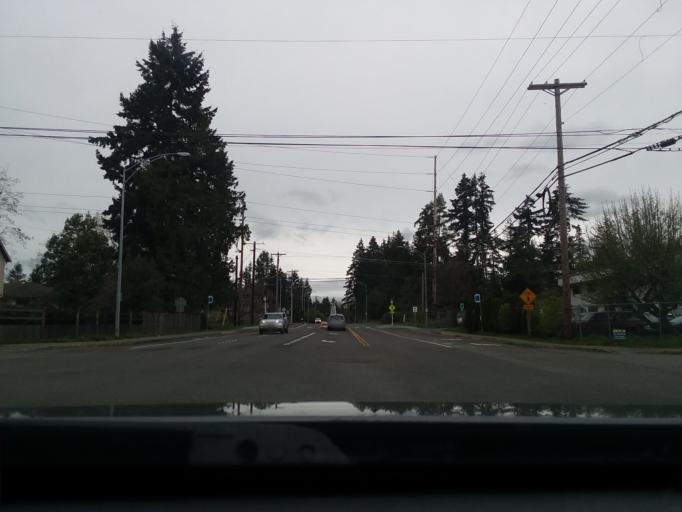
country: US
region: Washington
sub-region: Snohomish County
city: Lynnwood
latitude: 47.8100
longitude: -122.3031
